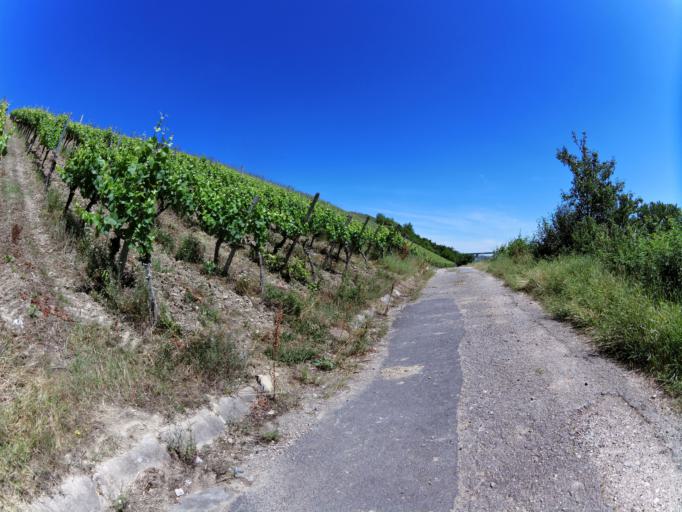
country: DE
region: Bavaria
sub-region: Regierungsbezirk Unterfranken
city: Frickenhausen
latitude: 49.6710
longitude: 10.1054
